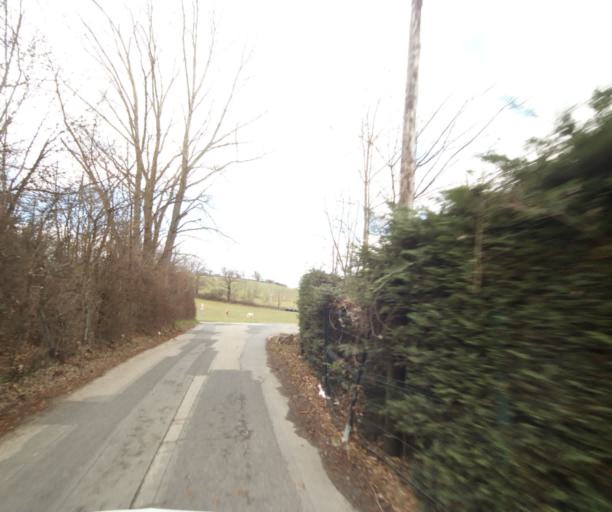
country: FR
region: Rhone-Alpes
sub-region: Departement de la Loire
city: Sorbiers
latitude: 45.4761
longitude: 4.4476
